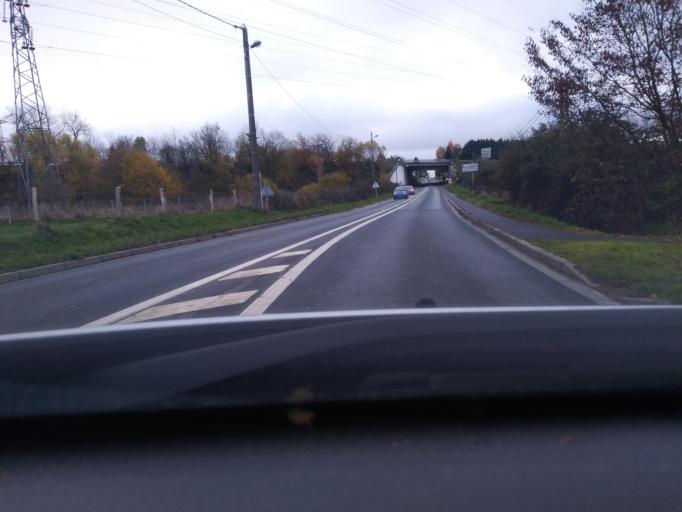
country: FR
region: Haute-Normandie
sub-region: Departement de la Seine-Maritime
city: La Vaupaliere
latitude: 49.4919
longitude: 0.9970
